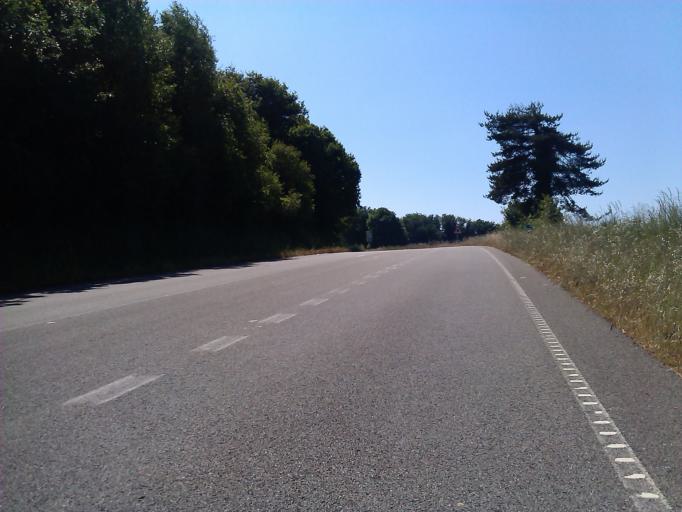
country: ES
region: Galicia
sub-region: Provincia de Lugo
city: Samos
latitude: 42.7347
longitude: -7.3570
